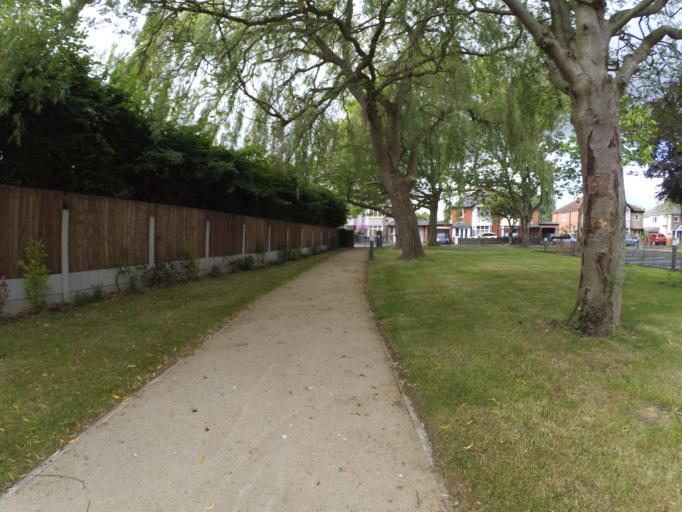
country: GB
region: England
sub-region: Warwickshire
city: Rugby
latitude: 52.3686
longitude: -1.2437
